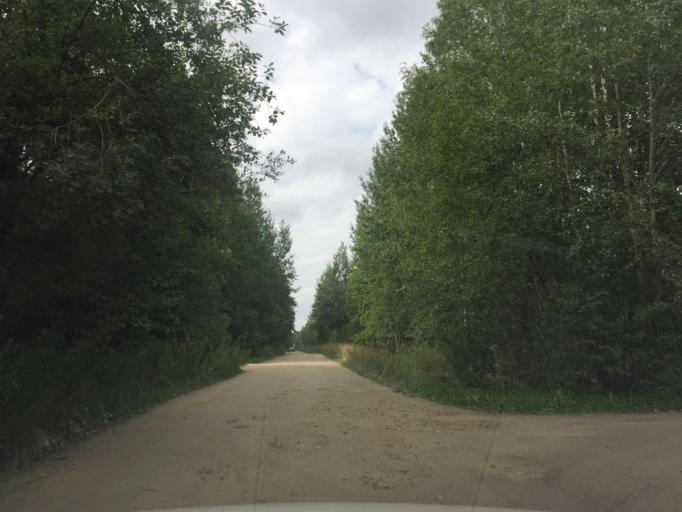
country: RU
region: Leningrad
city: Rozhdestveno
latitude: 59.2984
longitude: 30.0213
